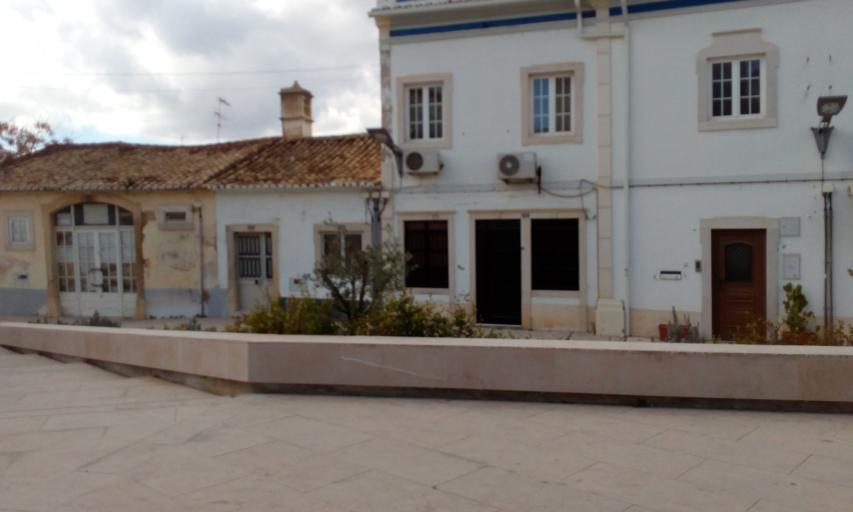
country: PT
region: Faro
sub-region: Loule
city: Loule
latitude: 37.1396
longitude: -8.0245
